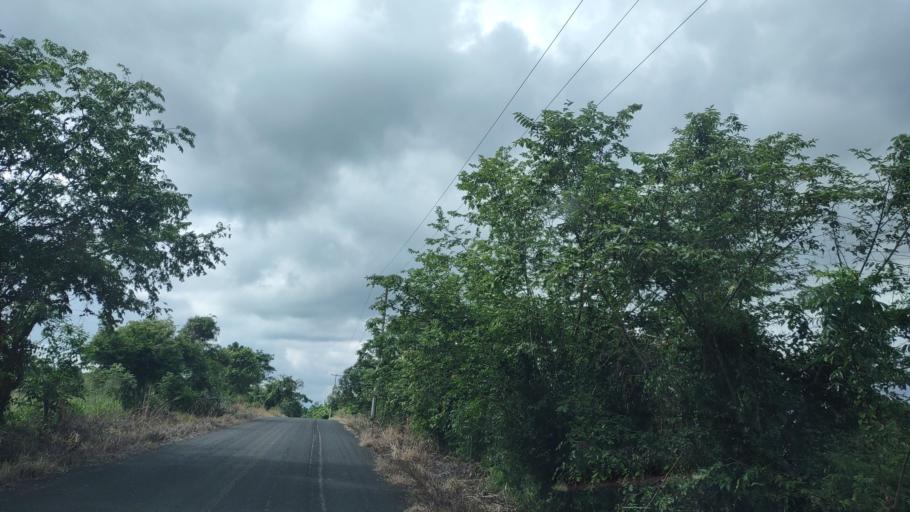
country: MX
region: Veracruz
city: Gutierrez Zamora
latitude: 20.2988
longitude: -97.1345
